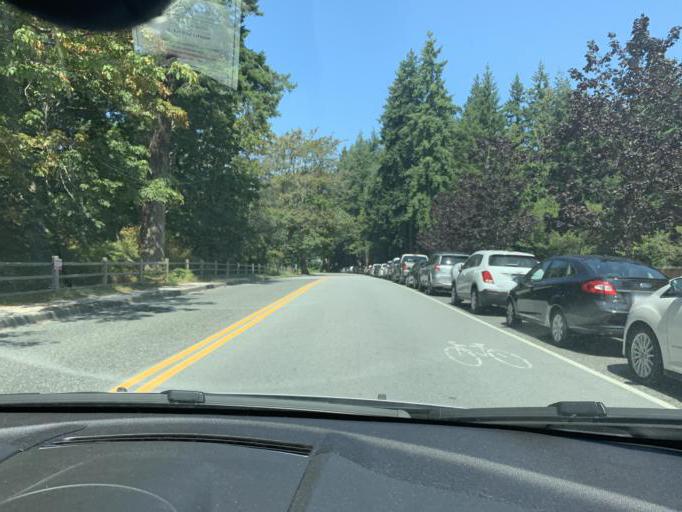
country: CA
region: British Columbia
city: West End
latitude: 49.2581
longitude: -123.2543
